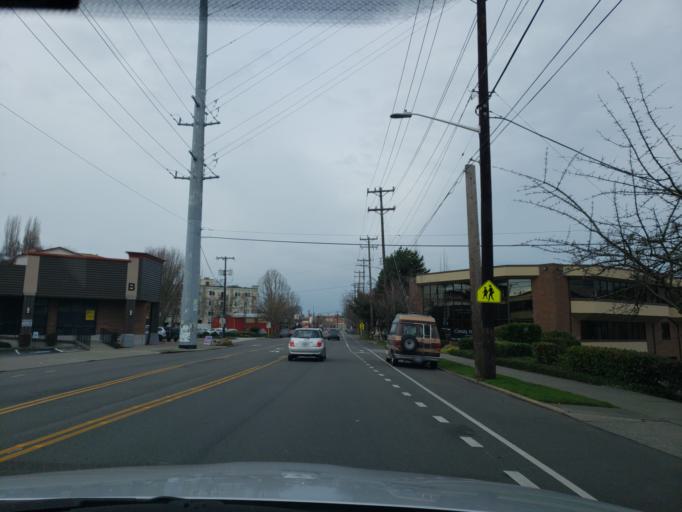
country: US
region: Washington
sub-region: King County
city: Seattle
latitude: 47.6484
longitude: -122.3546
